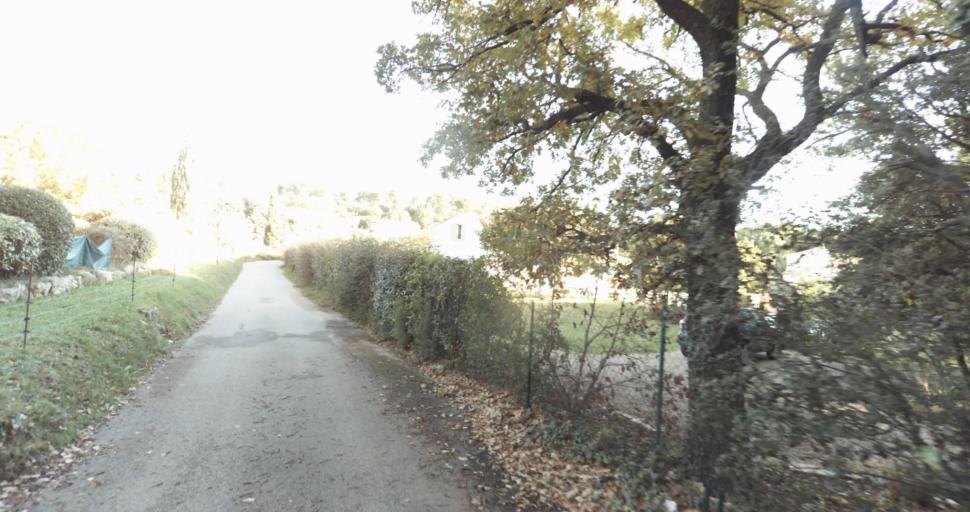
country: FR
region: Provence-Alpes-Cote d'Azur
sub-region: Departement des Bouches-du-Rhone
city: Venelles
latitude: 43.6024
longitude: 5.4720
